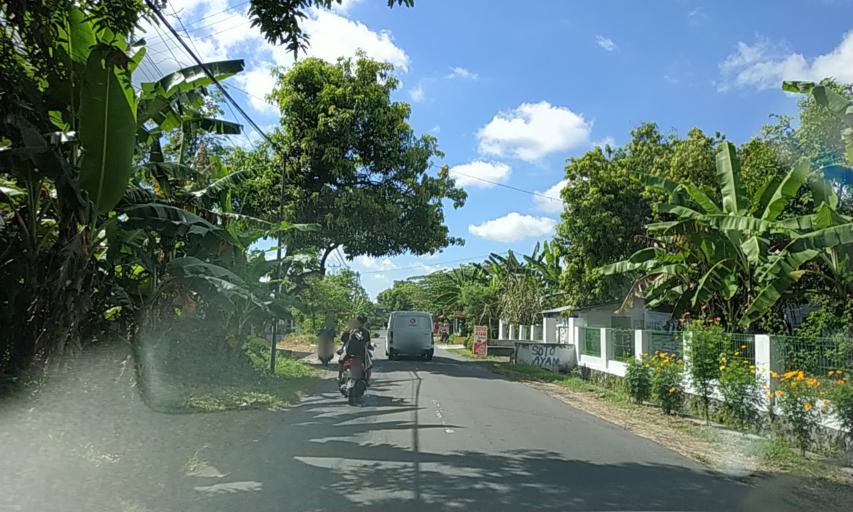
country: ID
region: Central Java
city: Trucuk
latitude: -7.6941
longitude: 110.6485
